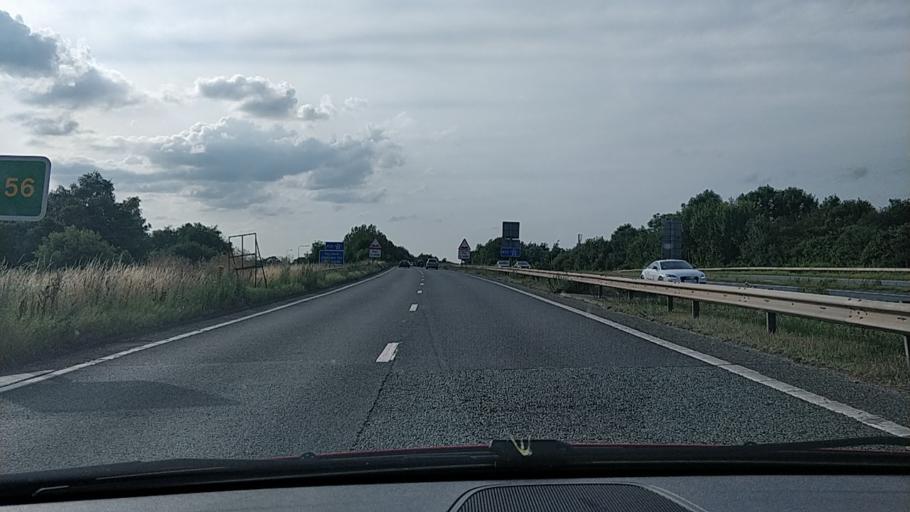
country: GB
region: England
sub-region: Cheshire West and Chester
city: Guilden Sutton
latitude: 53.2097
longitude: -2.8487
